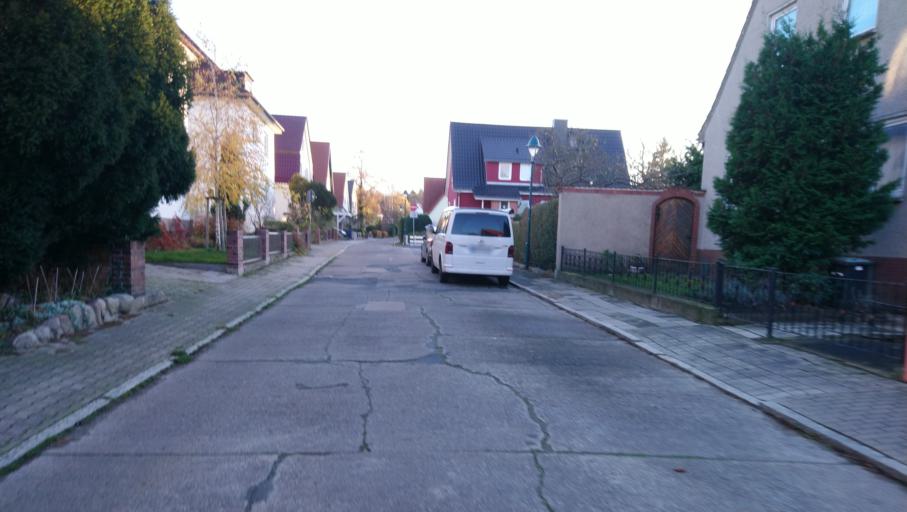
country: DE
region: Mecklenburg-Vorpommern
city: Kritzmow
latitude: 54.0865
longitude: 12.0827
